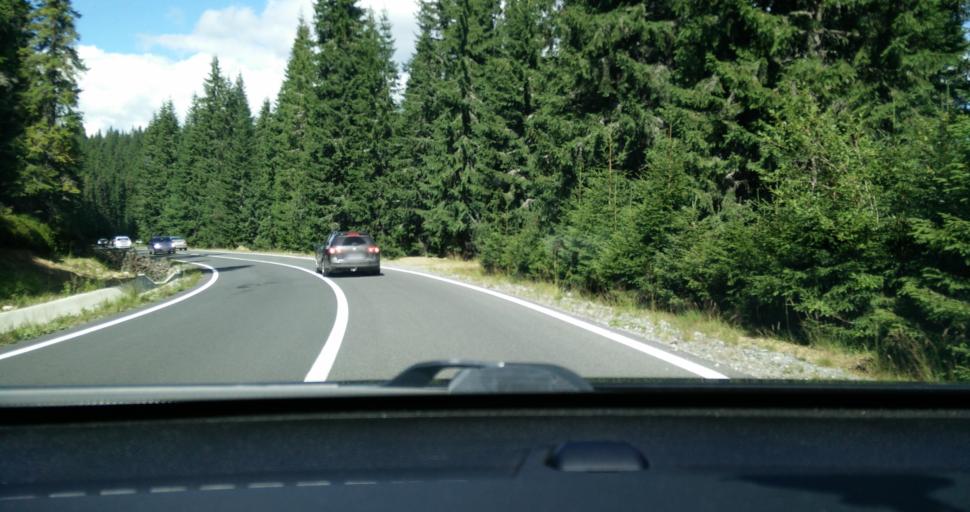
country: RO
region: Hunedoara
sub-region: Oras Petrila
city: Petrila
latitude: 45.4793
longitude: 23.6383
